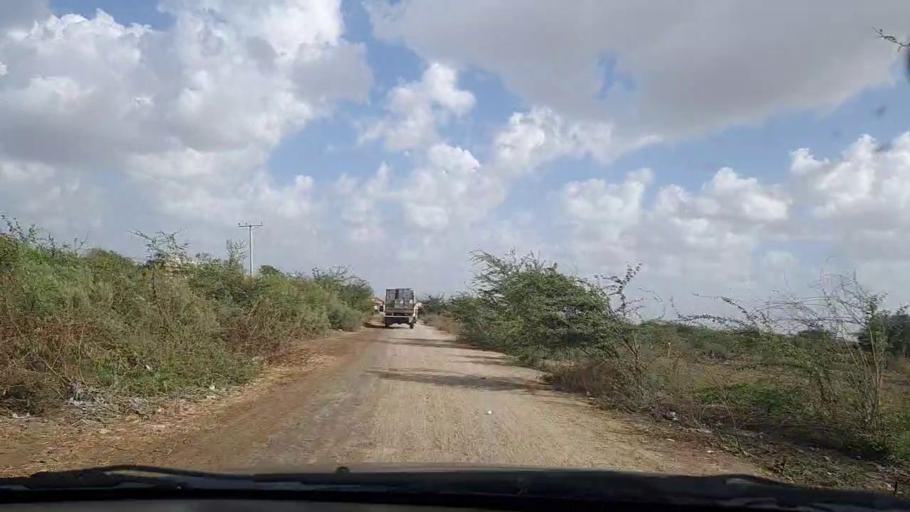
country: PK
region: Sindh
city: Keti Bandar
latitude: 24.0914
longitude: 67.6135
